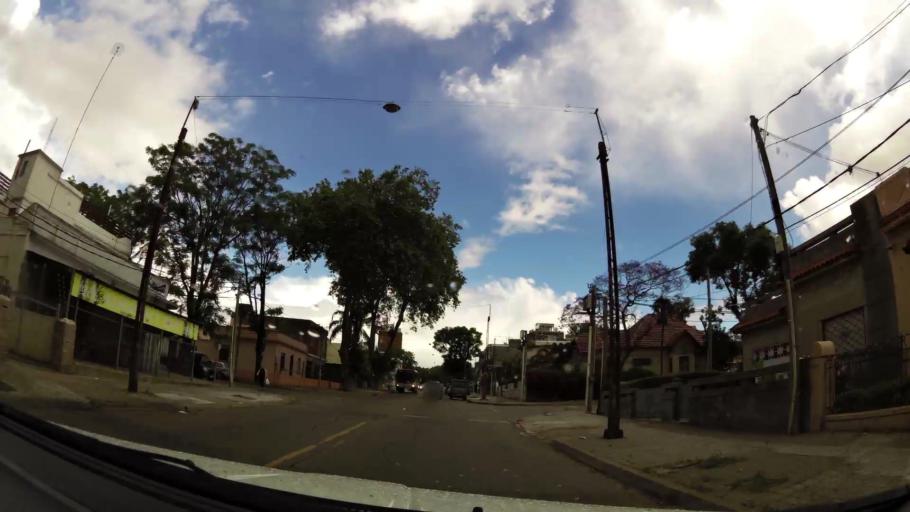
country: UY
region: Montevideo
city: Montevideo
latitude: -34.8615
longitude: -56.1783
